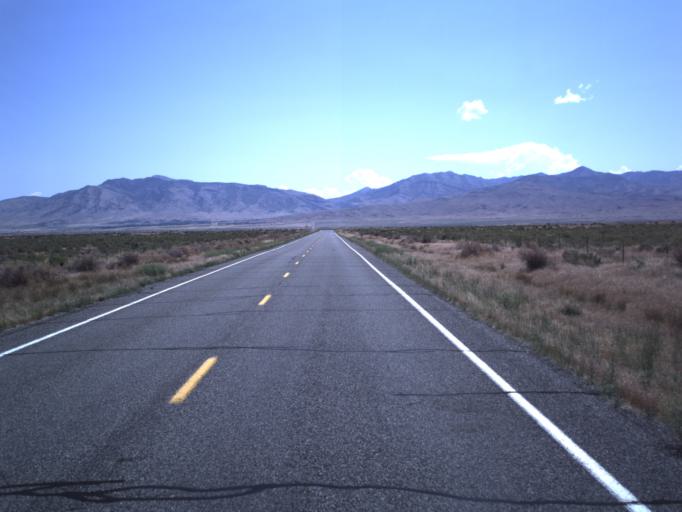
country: US
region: Utah
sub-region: Millard County
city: Delta
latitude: 39.3534
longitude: -112.4773
